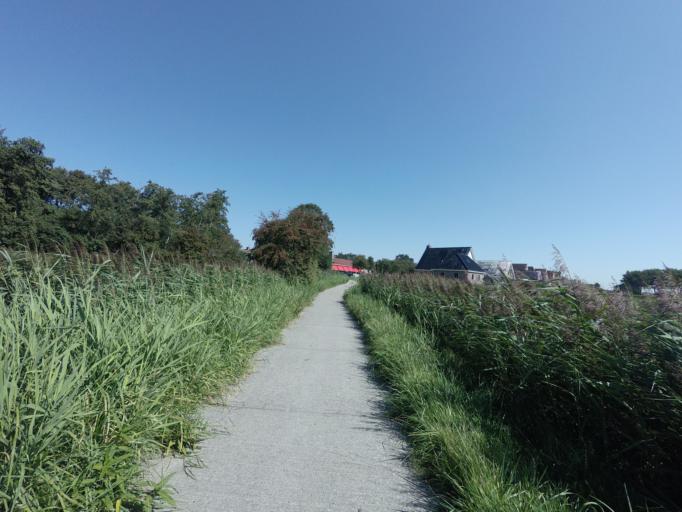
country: NL
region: Friesland
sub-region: Gemeente Dongeradeel
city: Anjum
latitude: 53.4009
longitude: 6.0816
